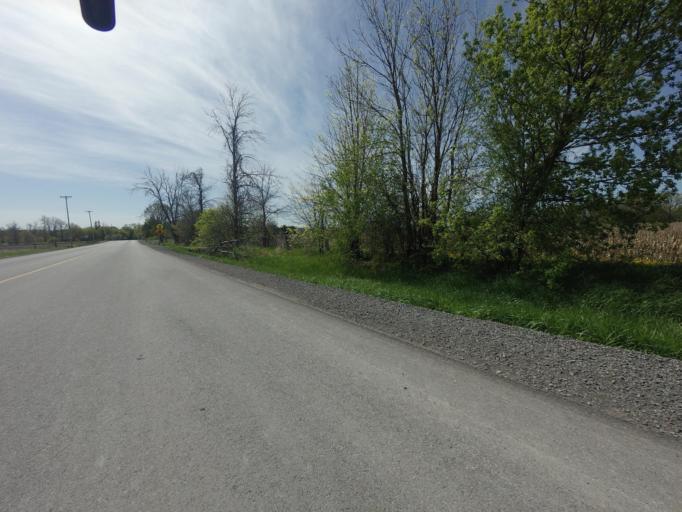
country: CA
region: Ontario
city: Arnprior
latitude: 45.4000
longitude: -76.1994
